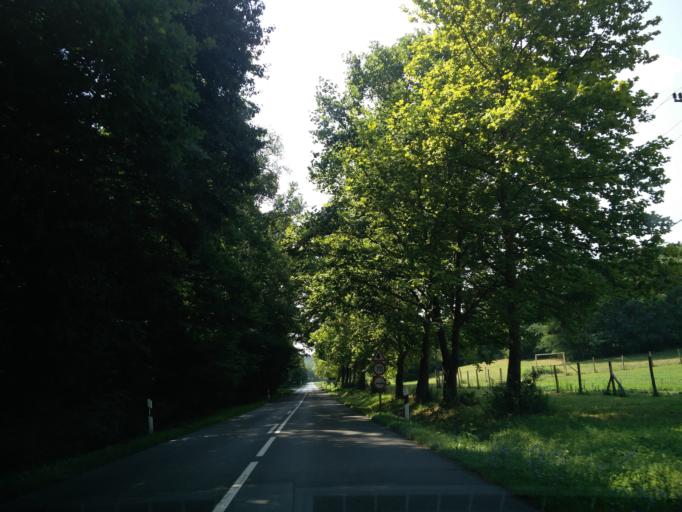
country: HU
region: Zala
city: Zalaegerszeg
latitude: 46.8093
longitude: 16.8247
